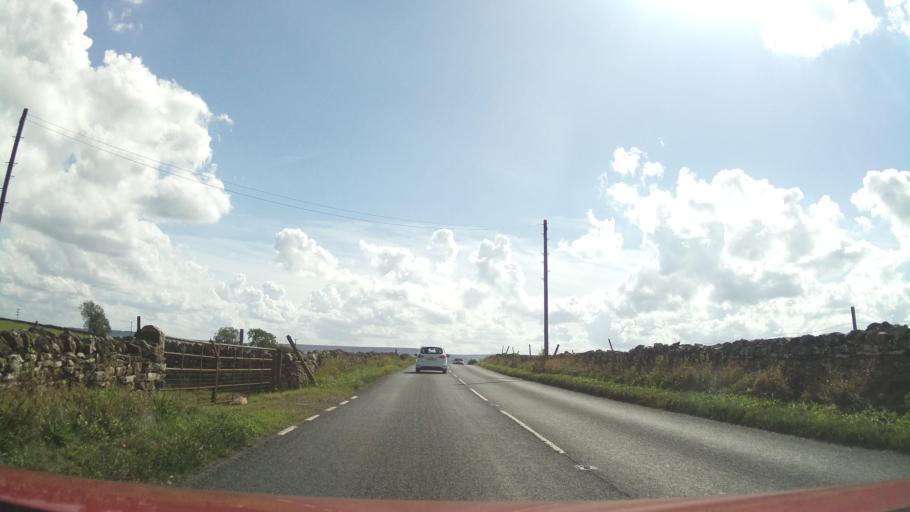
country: GB
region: England
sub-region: North Yorkshire
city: Leyburn
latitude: 54.3213
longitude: -1.8216
